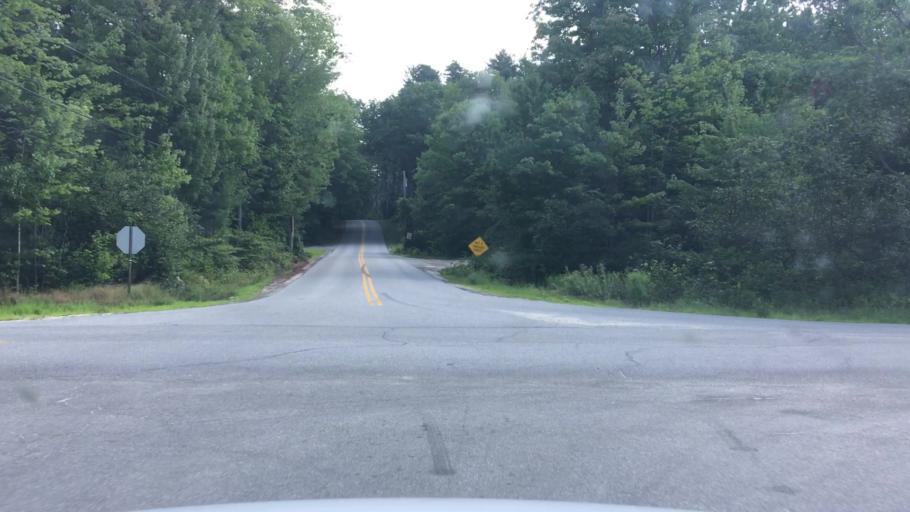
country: US
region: Maine
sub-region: Cumberland County
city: Raymond
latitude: 43.9272
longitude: -70.5218
